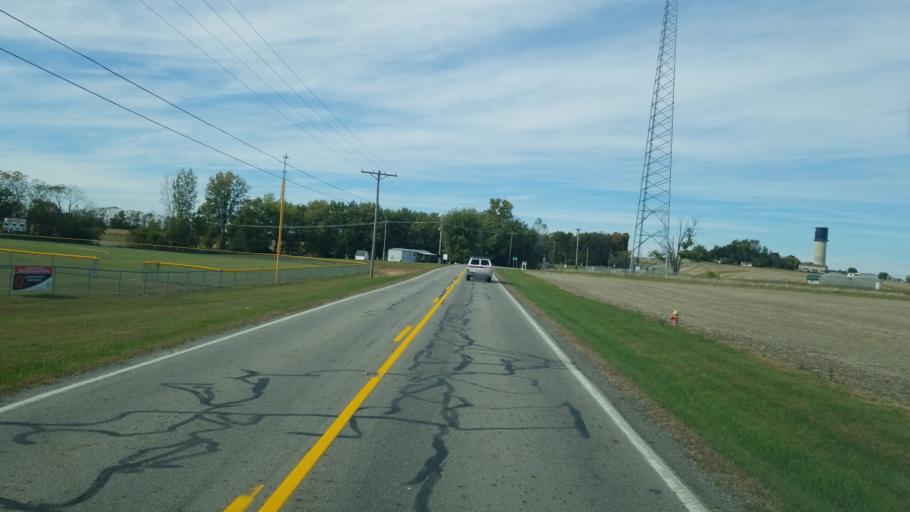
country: US
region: Ohio
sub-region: Highland County
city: Leesburg
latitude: 39.3306
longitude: -83.5468
